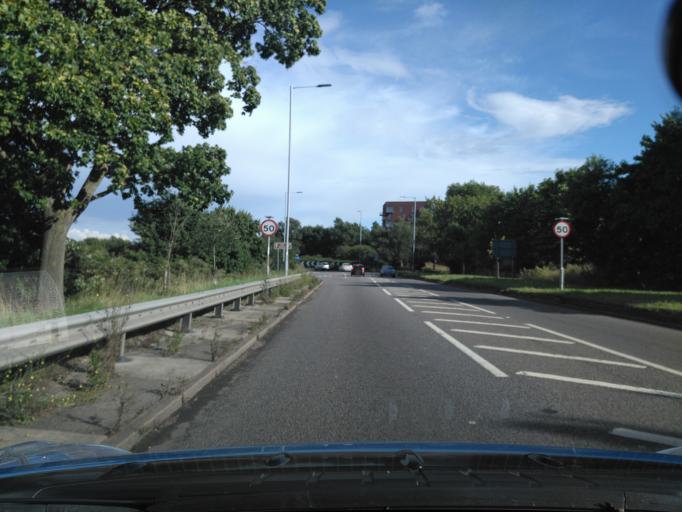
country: GB
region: England
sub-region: Hertfordshire
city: Elstree
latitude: 51.6251
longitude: -0.2891
